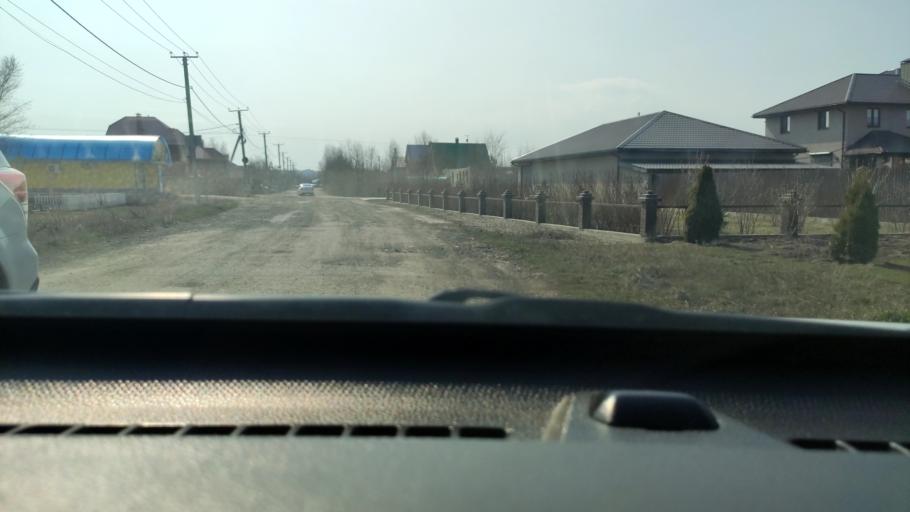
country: RU
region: Samara
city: Tol'yatti
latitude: 53.5569
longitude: 49.3703
